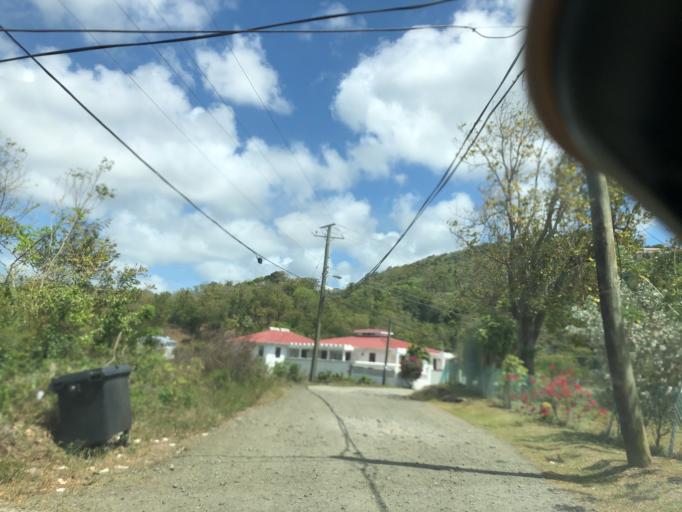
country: LC
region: Gros-Islet
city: Gros Islet
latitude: 14.0636
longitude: -60.9722
